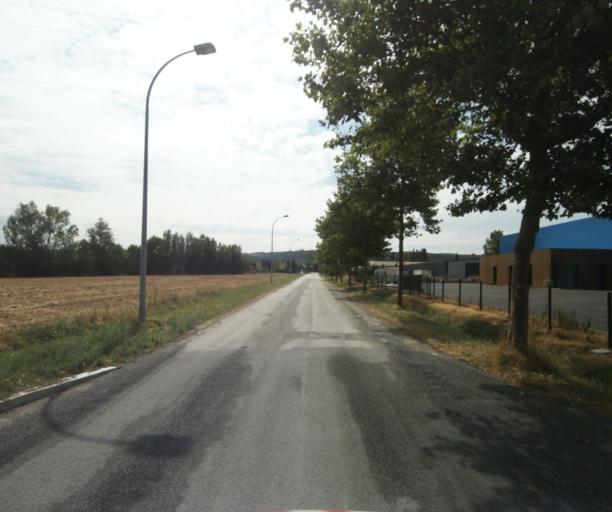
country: FR
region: Midi-Pyrenees
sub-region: Departement de la Haute-Garonne
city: Revel
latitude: 43.4571
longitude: 1.9847
